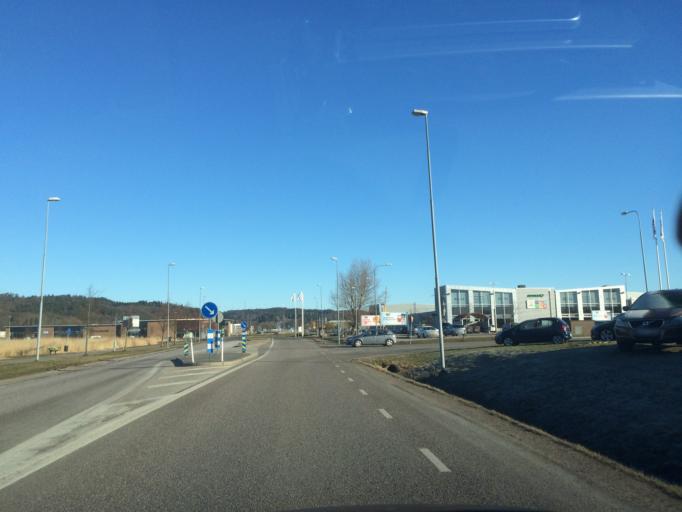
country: SE
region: Halland
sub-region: Kungsbacka Kommun
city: Kungsbacka
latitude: 57.5104
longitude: 12.0809
